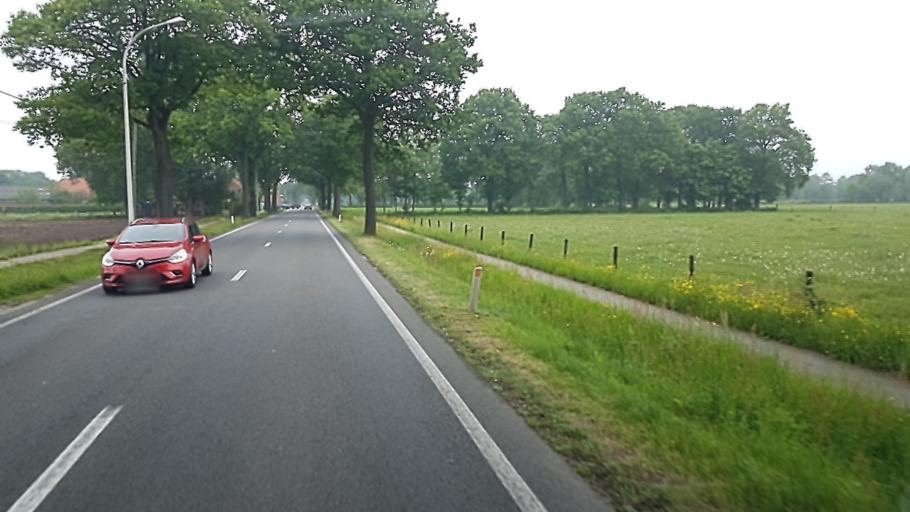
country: BE
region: Flanders
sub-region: Provincie Antwerpen
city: Brecht
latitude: 51.3616
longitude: 4.6208
